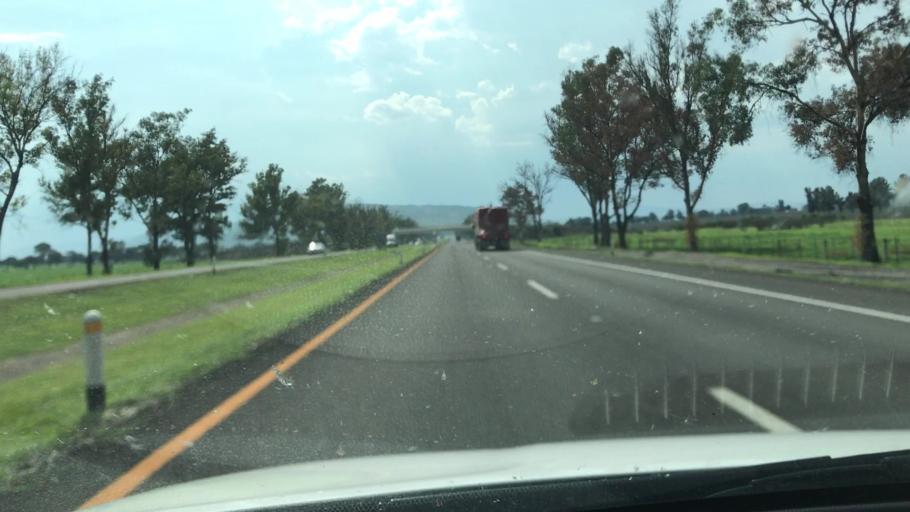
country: MX
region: Jalisco
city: Ocotlan
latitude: 20.3850
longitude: -102.7074
